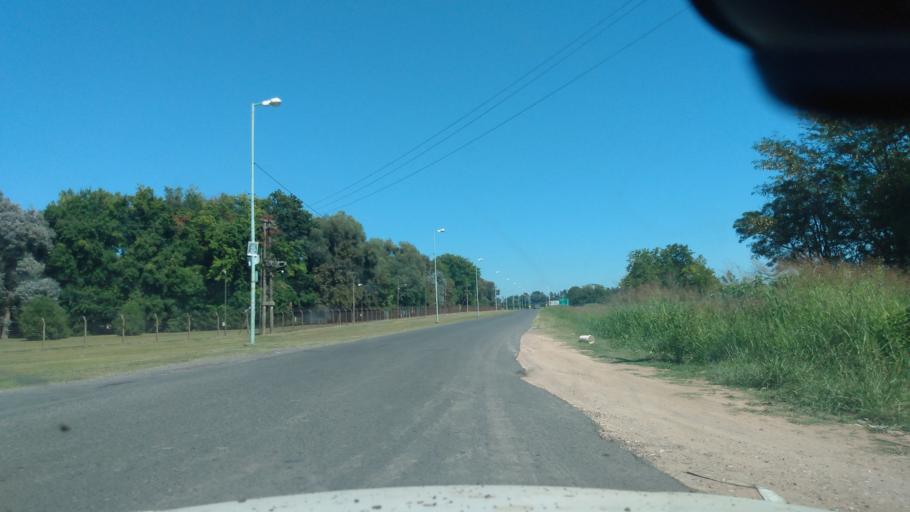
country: AR
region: Buenos Aires
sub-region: Partido de Lujan
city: Lujan
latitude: -34.5097
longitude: -59.0867
